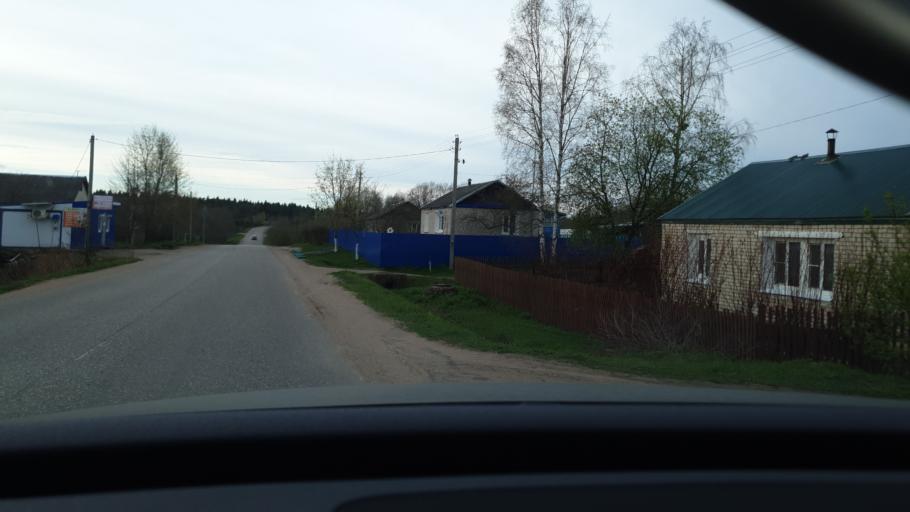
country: RU
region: Tverskaya
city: Berezayka
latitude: 58.0464
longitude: 33.7781
